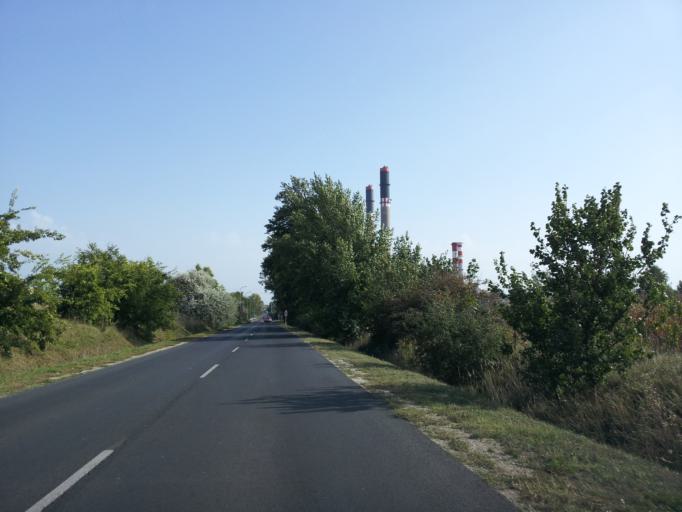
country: HU
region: Pest
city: Szazhalombatta
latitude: 47.3356
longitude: 18.9134
